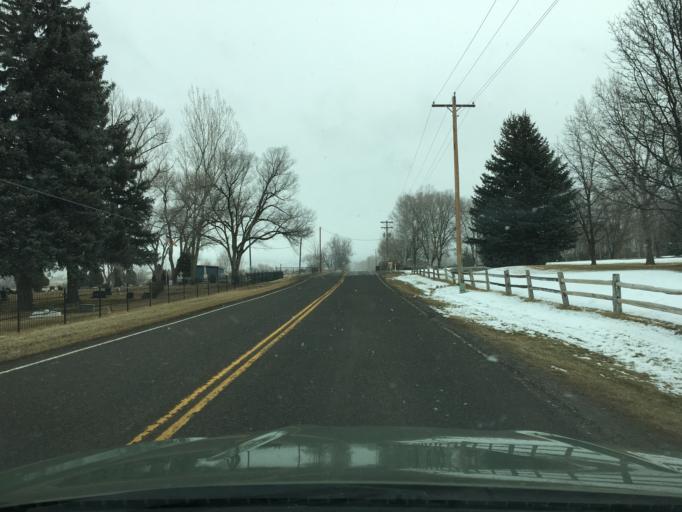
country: US
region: Colorado
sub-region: Montrose County
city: Montrose
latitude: 38.4817
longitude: -107.8525
